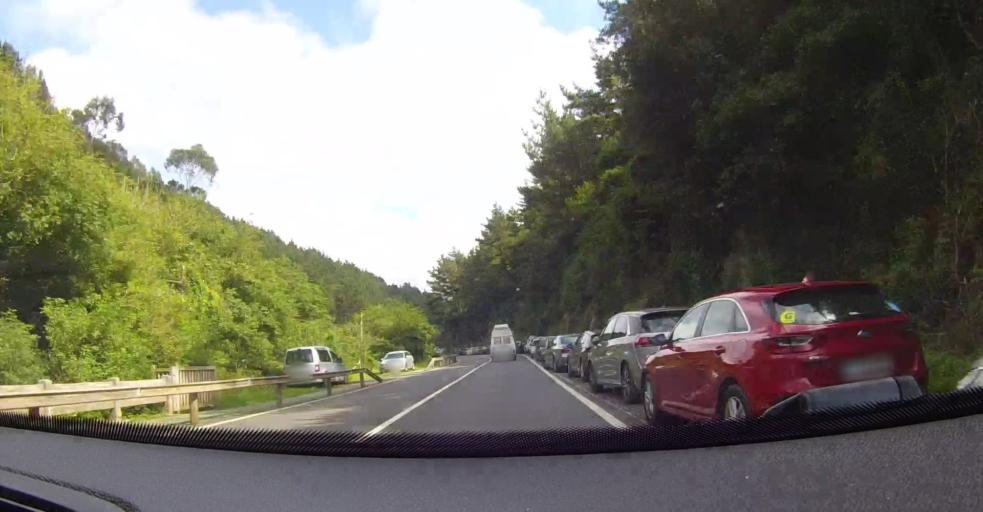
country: ES
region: Basque Country
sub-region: Bizkaia
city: Elantxobe
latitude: 43.4041
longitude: -2.6512
